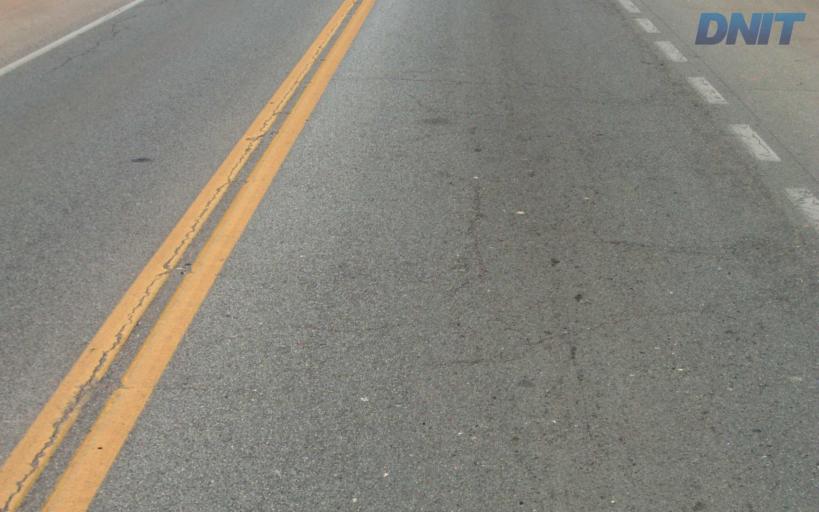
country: BR
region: Minas Gerais
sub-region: Barao De Cocais
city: Barao de Cocais
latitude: -19.7487
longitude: -43.4904
